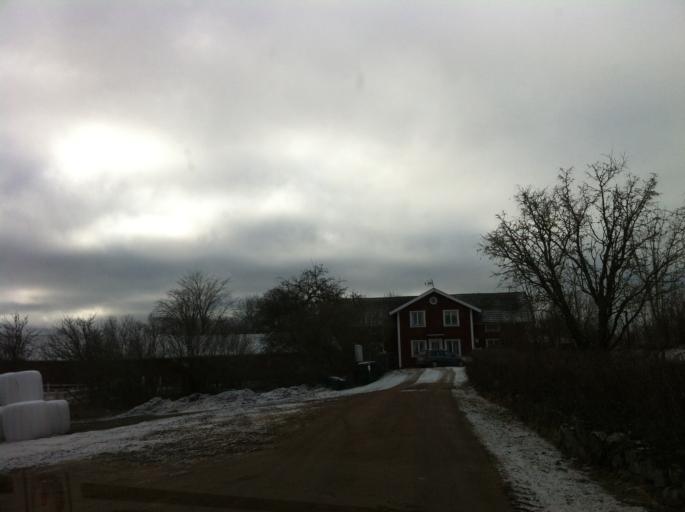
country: SE
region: Joenkoeping
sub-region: Eksjo Kommun
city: Mariannelund
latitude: 57.6137
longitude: 15.7064
